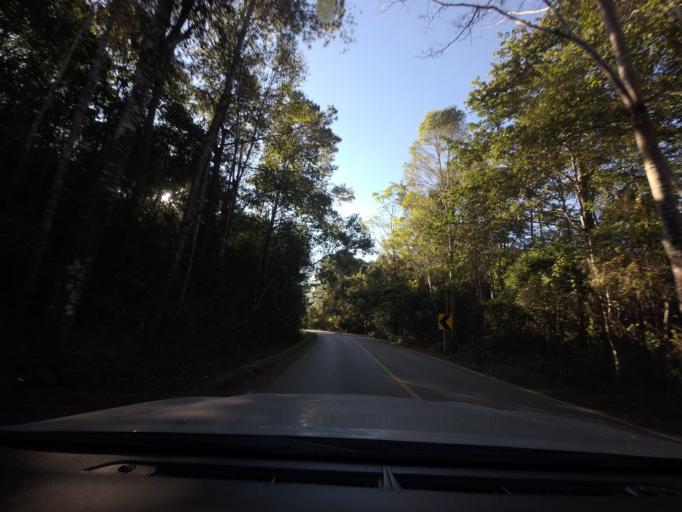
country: TH
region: Mae Hong Son
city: Mae Hi
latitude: 19.2711
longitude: 98.6278
